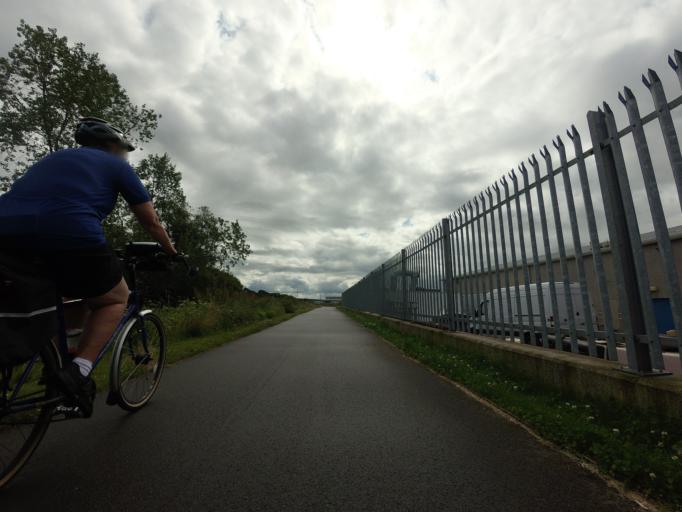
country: GB
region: Scotland
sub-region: Moray
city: Elgin
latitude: 57.6514
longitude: -3.2910
